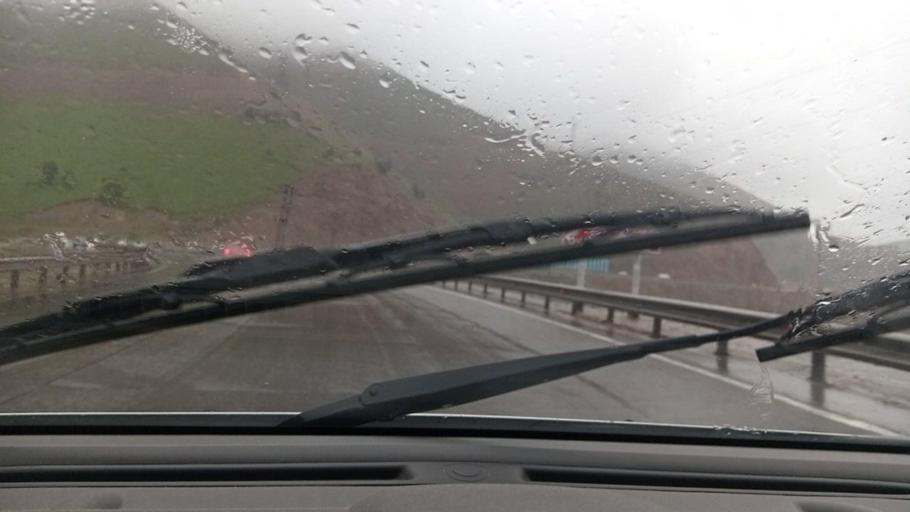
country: UZ
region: Toshkent
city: Angren
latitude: 41.0938
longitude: 70.5268
